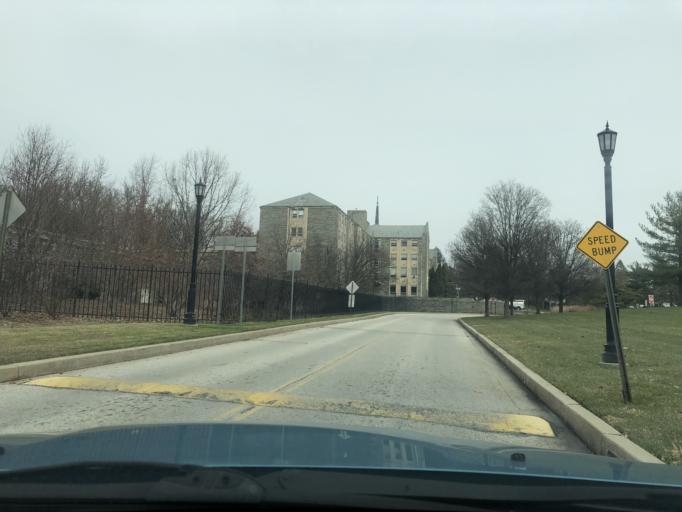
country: US
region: Pennsylvania
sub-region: Delaware County
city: Radnor
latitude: 40.0393
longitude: -75.3425
